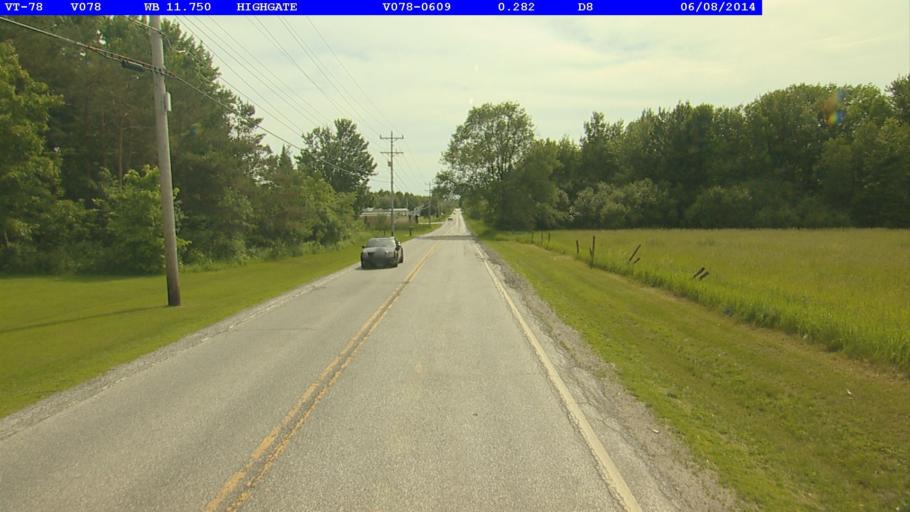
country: US
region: Vermont
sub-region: Franklin County
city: Swanton
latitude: 44.9282
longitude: -73.0937
